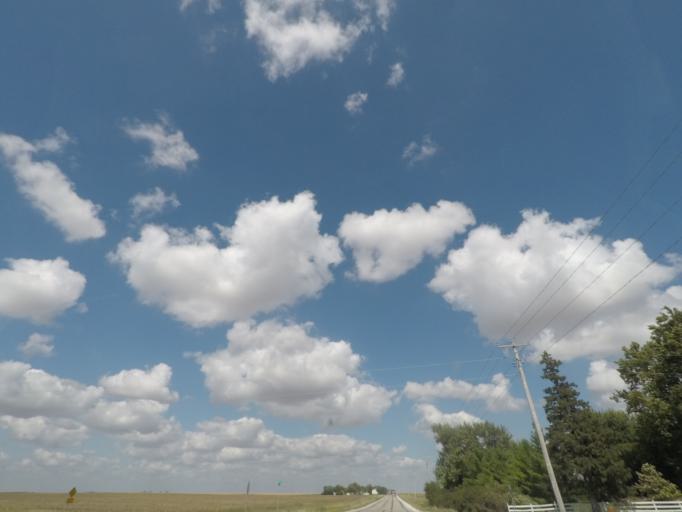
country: US
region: Iowa
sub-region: Story County
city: Nevada
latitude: 42.0631
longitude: -93.4056
